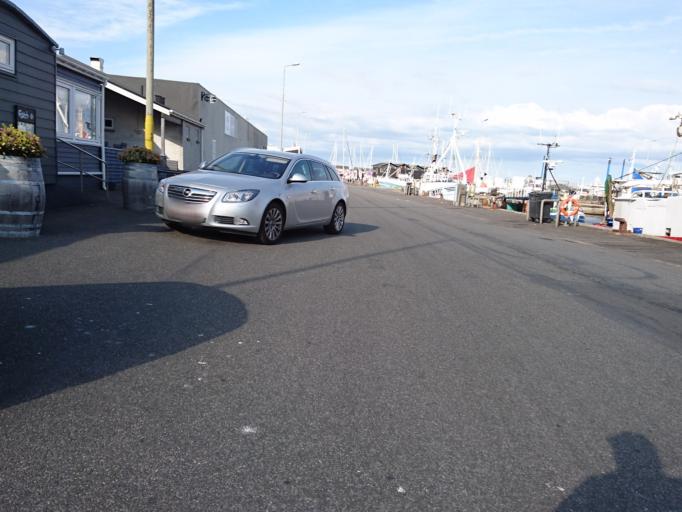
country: DK
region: North Denmark
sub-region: Frederikshavn Kommune
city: Skagen
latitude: 57.7175
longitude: 10.5848
